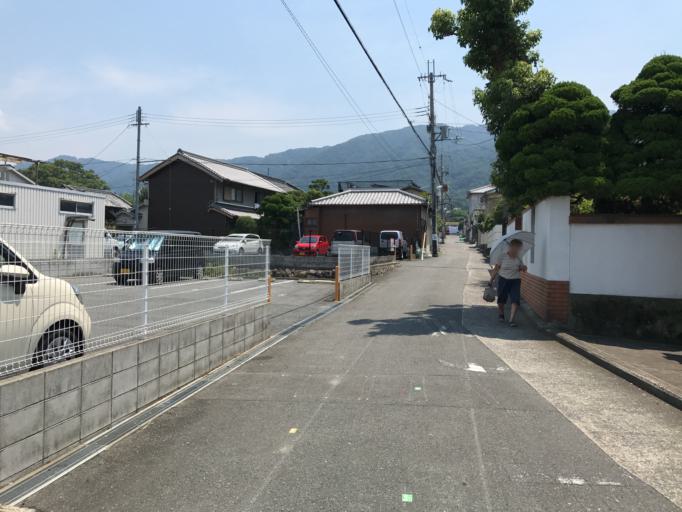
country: JP
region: Osaka
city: Yao
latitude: 34.6179
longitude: 135.6336
